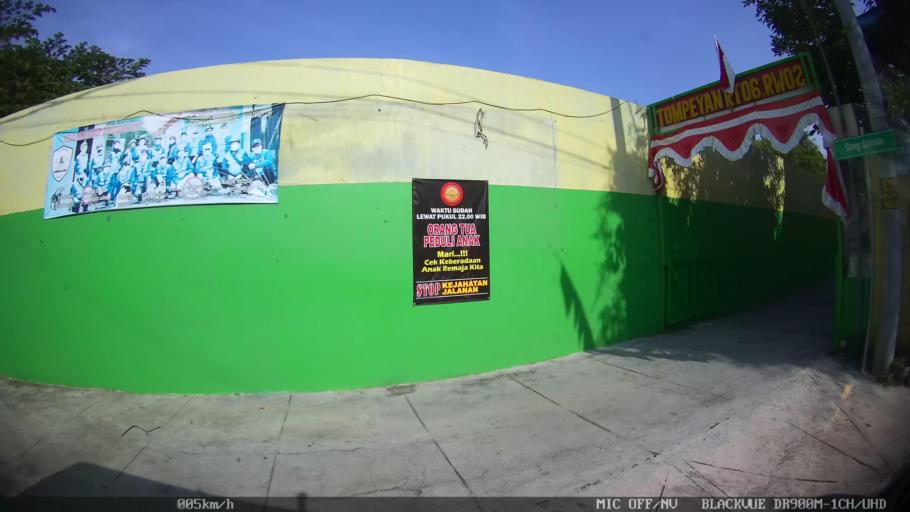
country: ID
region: Daerah Istimewa Yogyakarta
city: Yogyakarta
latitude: -7.7869
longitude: 110.3535
